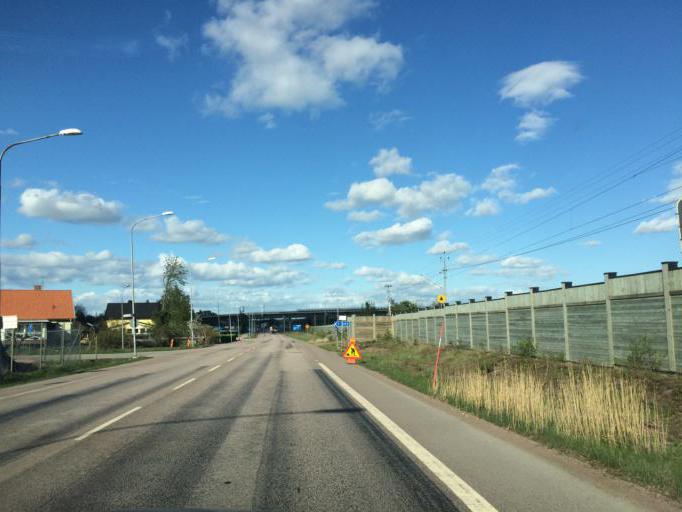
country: SE
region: Vaestmanland
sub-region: Hallstahammars Kommun
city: Kolback
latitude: 59.5587
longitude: 16.2201
